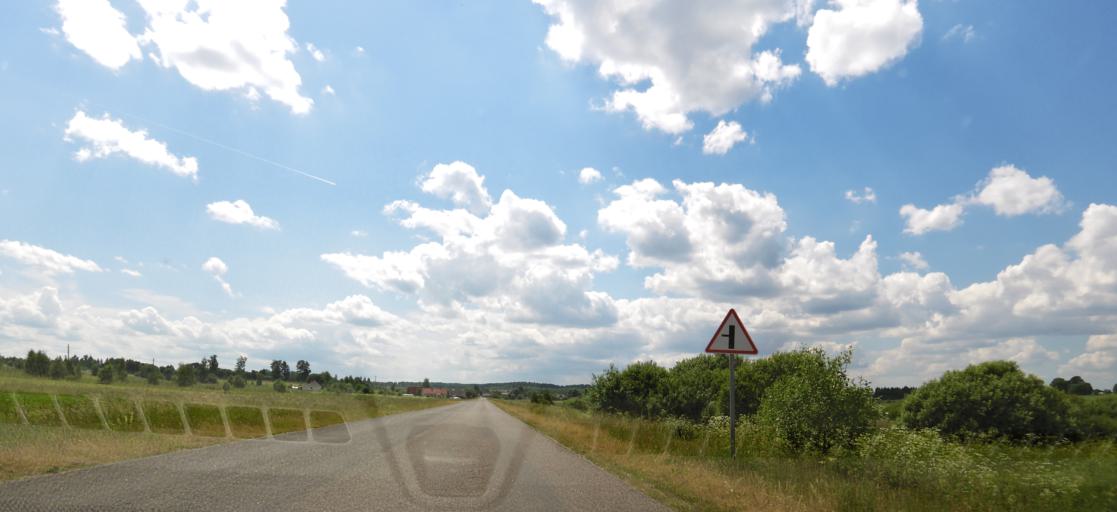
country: LT
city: Skaidiskes
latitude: 54.5491
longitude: 25.6555
